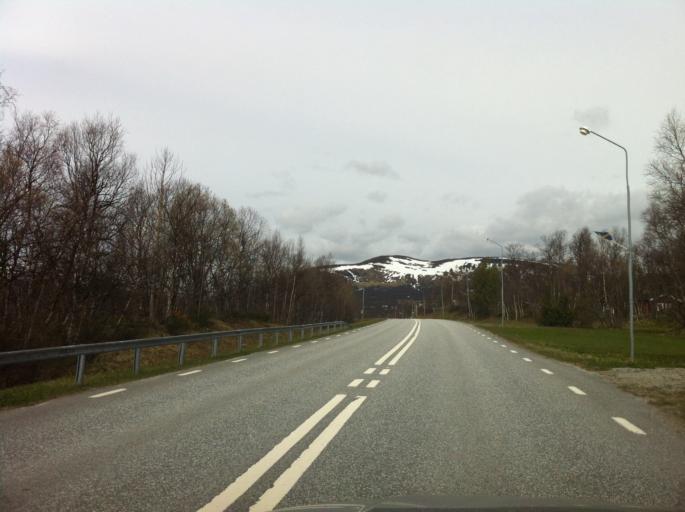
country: NO
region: Sor-Trondelag
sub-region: Tydal
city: Aas
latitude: 62.5423
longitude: 12.3357
